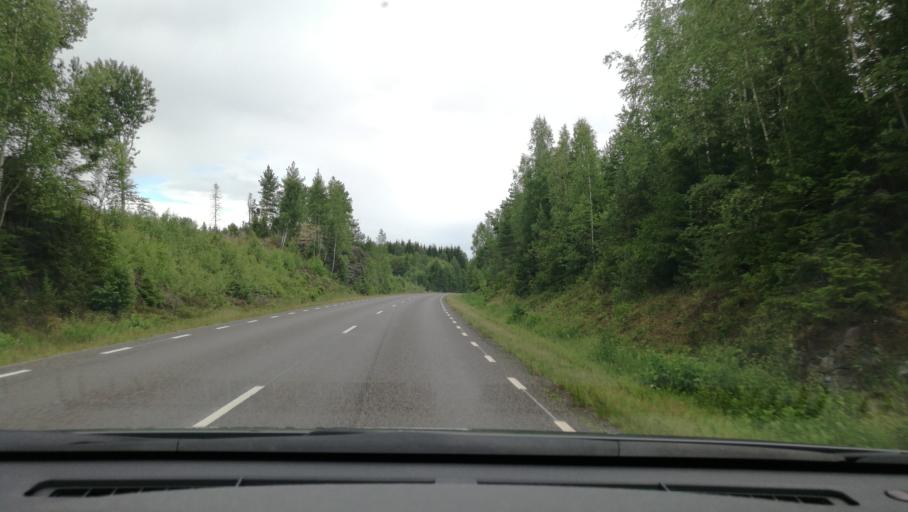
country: SE
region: OEstergoetland
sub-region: Norrkopings Kommun
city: Svartinge
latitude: 58.7861
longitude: 15.9641
